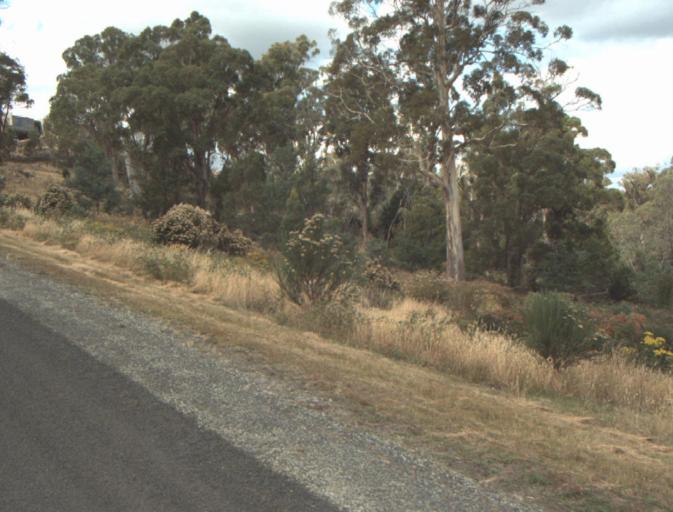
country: AU
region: Tasmania
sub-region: Launceston
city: Mayfield
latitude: -41.3010
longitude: 147.0432
